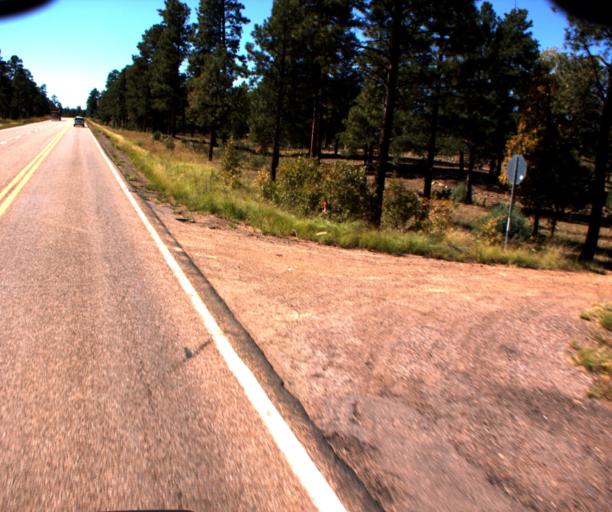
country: US
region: Arizona
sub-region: Navajo County
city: Heber-Overgaard
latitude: 34.4086
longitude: -110.6641
